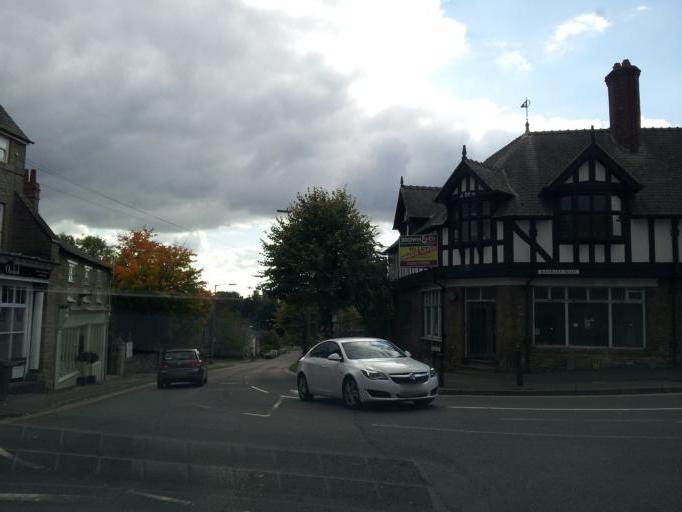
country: GB
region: England
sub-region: Northamptonshire
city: Brackley
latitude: 52.0262
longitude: -1.1501
